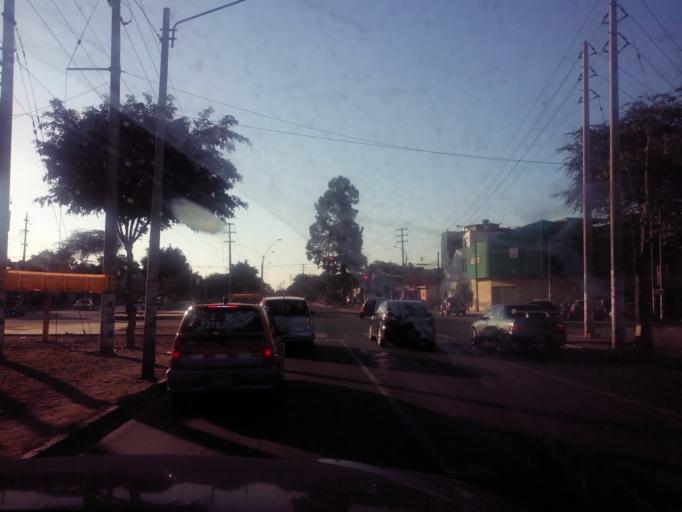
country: PE
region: Ica
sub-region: Provincia de Ica
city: Ica
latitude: -14.0556
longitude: -75.7440
